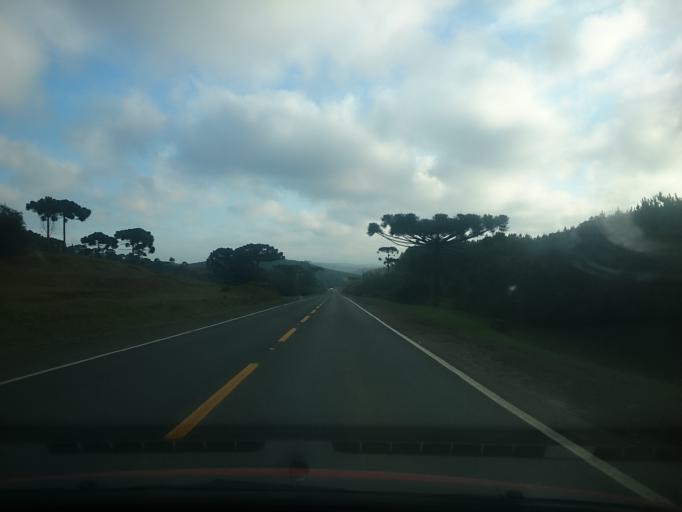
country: BR
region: Santa Catarina
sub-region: Lages
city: Lages
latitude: -28.0526
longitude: -50.5684
